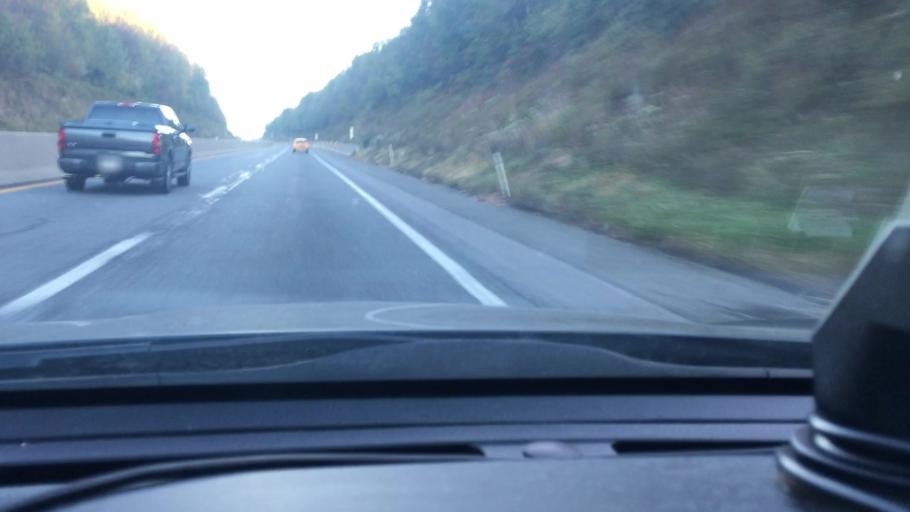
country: US
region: Pennsylvania
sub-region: Carbon County
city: Weissport East
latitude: 40.9241
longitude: -75.6461
